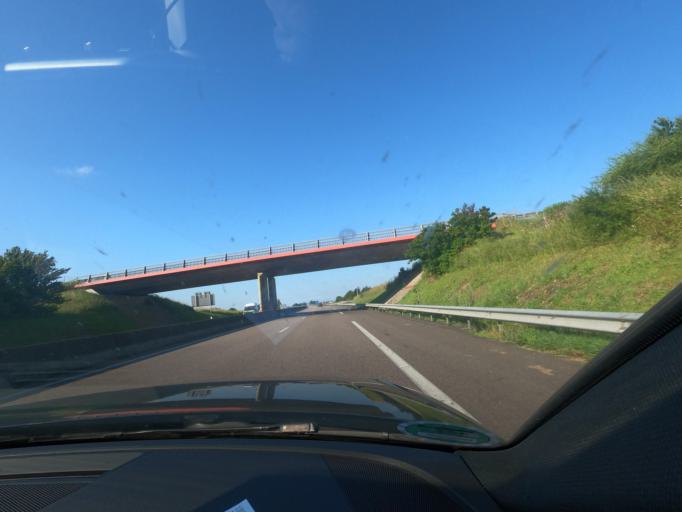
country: FR
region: Haute-Normandie
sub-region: Departement de la Seine-Maritime
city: Aumale
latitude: 49.7709
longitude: 1.7131
